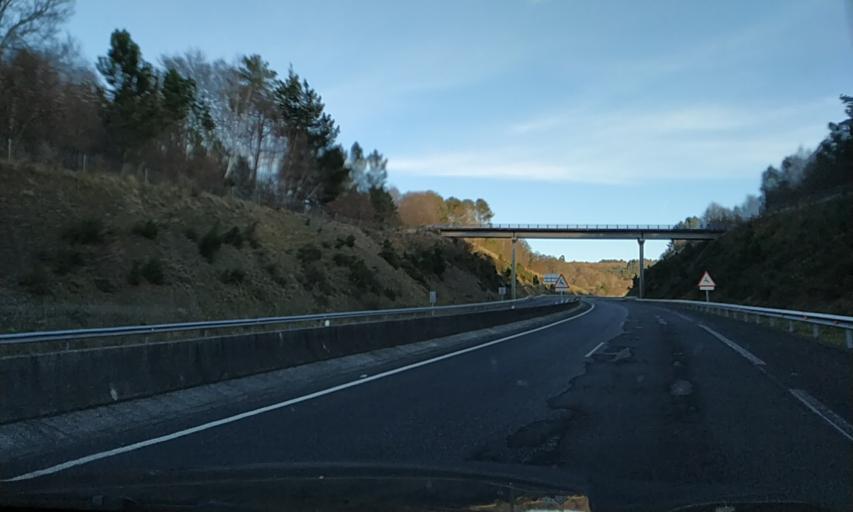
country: ES
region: Galicia
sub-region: Provincia de Pontevedra
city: Lalin
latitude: 42.6329
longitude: -8.1265
